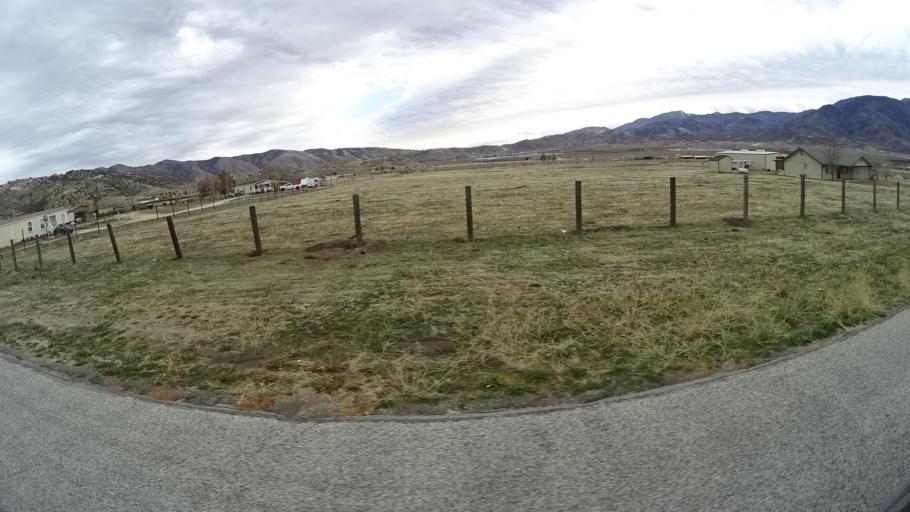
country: US
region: California
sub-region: Kern County
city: Stallion Springs
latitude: 35.1198
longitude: -118.6281
